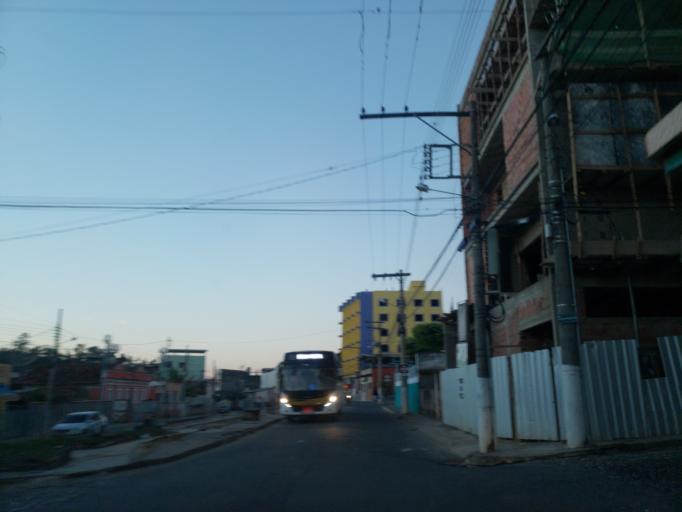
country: BR
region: Minas Gerais
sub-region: Sao Joao Nepomuceno
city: Sao Joao Nepomuceno
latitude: -21.5295
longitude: -43.0147
